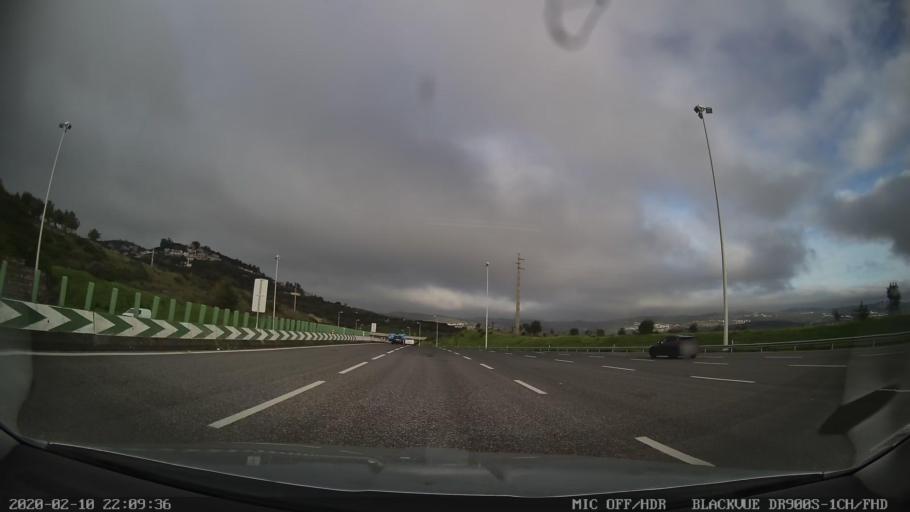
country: PT
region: Lisbon
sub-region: Odivelas
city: Ramada
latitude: 38.8207
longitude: -9.1878
